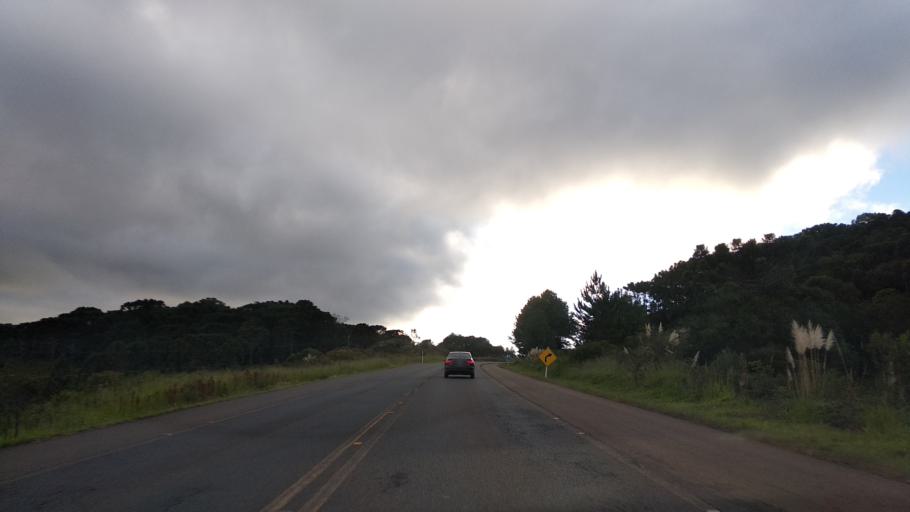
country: BR
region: Santa Catarina
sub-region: Curitibanos
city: Curitibanos
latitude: -27.5789
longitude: -50.7700
